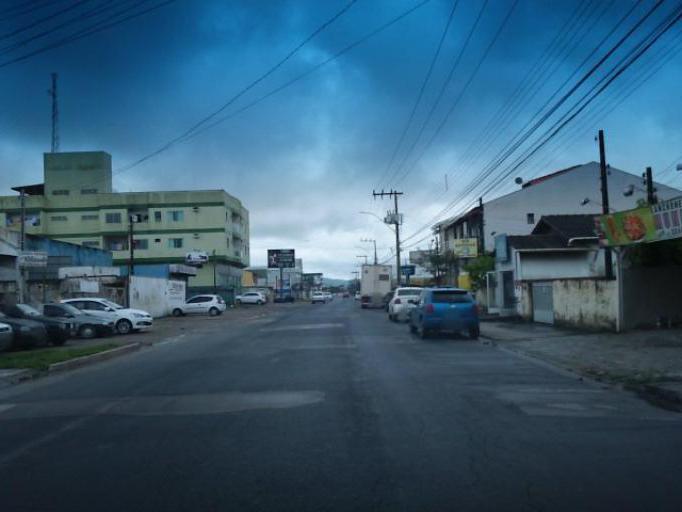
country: BR
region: Santa Catarina
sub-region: Itajai
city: Itajai
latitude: -26.9128
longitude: -48.7007
